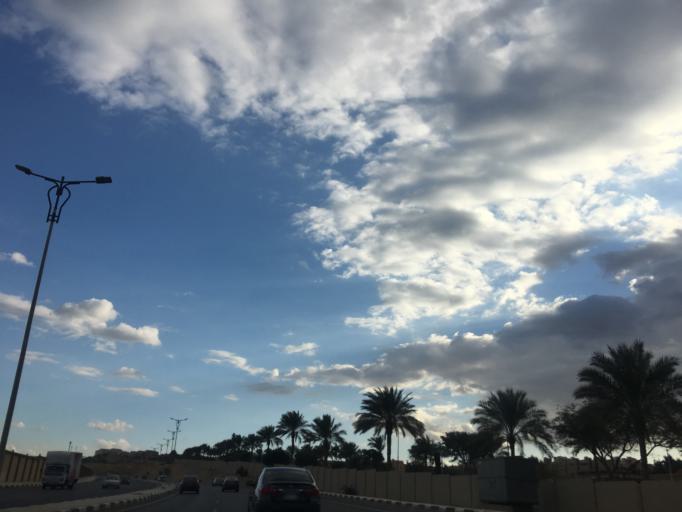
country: EG
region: Muhafazat al Qahirah
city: Cairo
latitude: 30.0351
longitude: 31.3066
